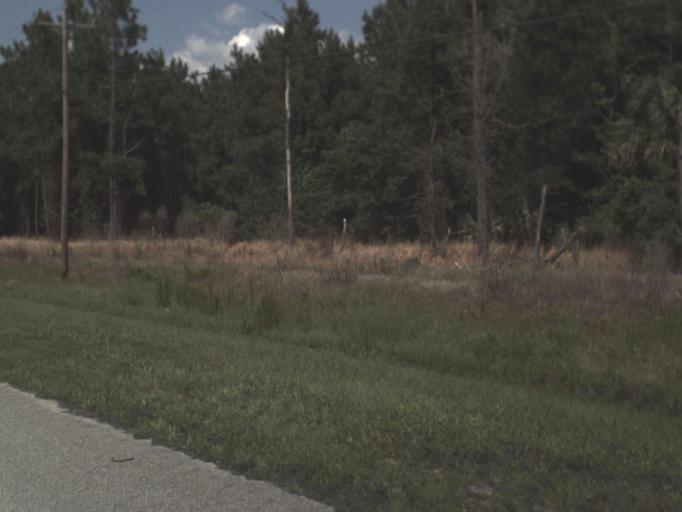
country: US
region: Florida
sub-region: Alachua County
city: Hawthorne
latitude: 29.5580
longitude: -82.0961
